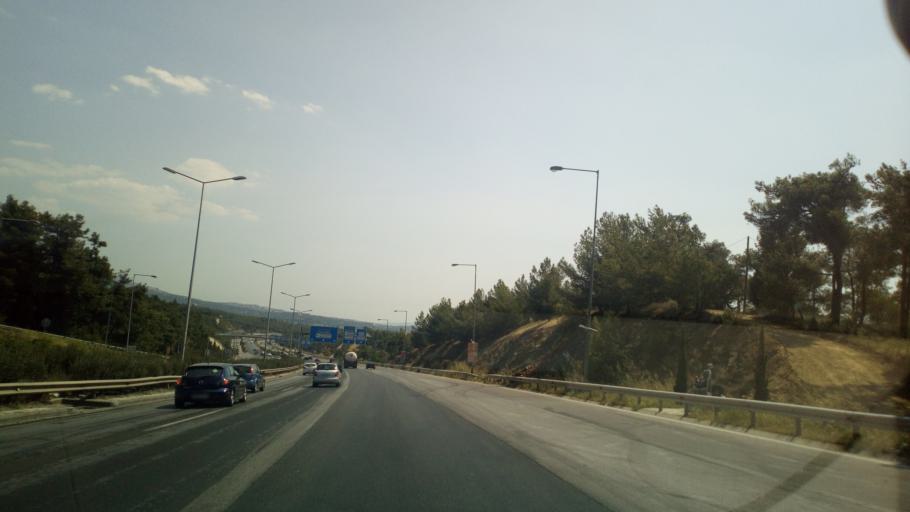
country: GR
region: Central Macedonia
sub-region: Nomos Thessalonikis
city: Agios Pavlos
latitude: 40.6318
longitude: 22.9736
